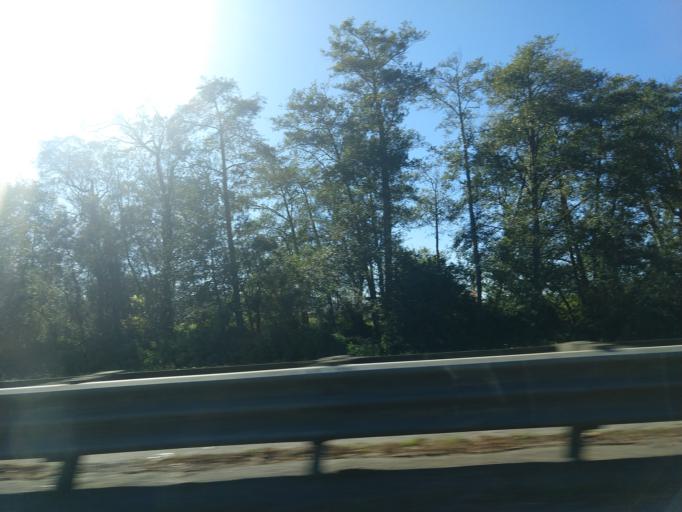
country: US
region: California
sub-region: Humboldt County
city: Fortuna
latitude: 40.5826
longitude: -124.1515
